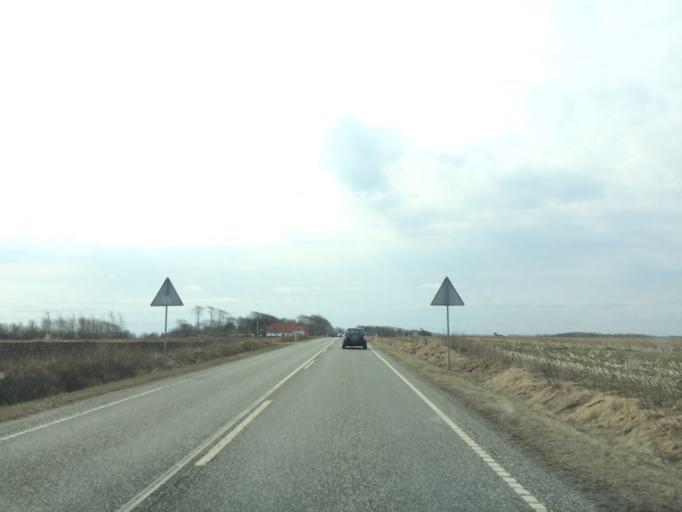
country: DK
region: Central Jutland
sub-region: Ringkobing-Skjern Kommune
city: Skjern
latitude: 56.0251
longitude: 8.5023
